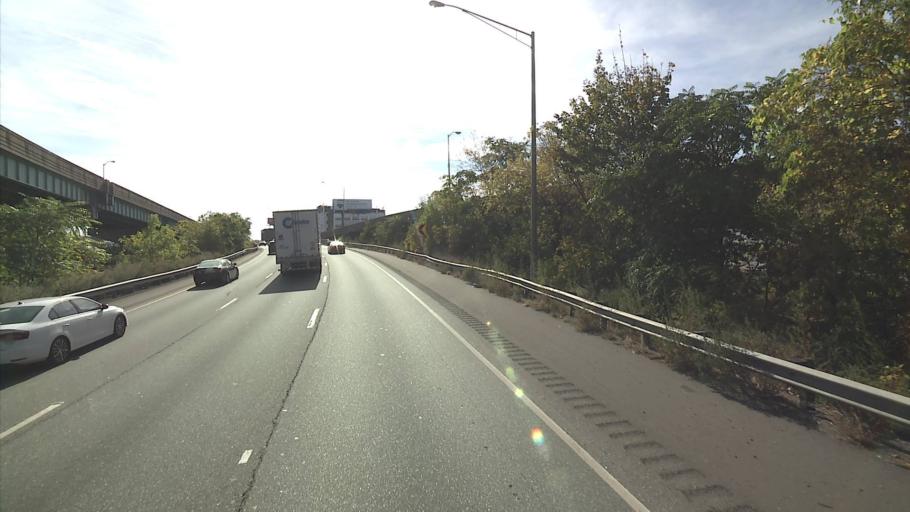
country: US
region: Connecticut
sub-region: Hartford County
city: Hartford
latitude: 41.7604
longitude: -72.7001
